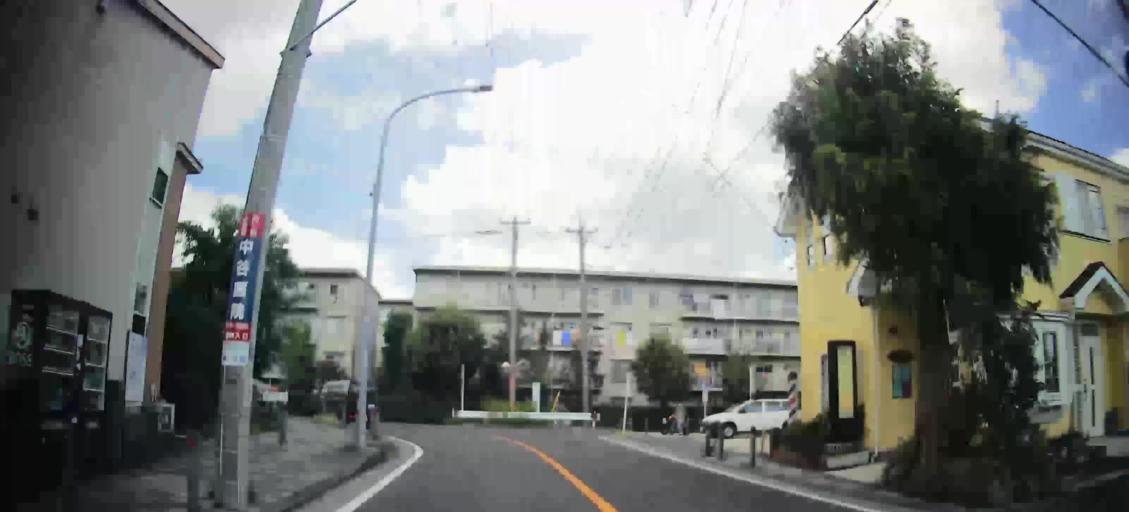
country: JP
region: Kanagawa
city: Yokohama
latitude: 35.4678
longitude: 139.5611
